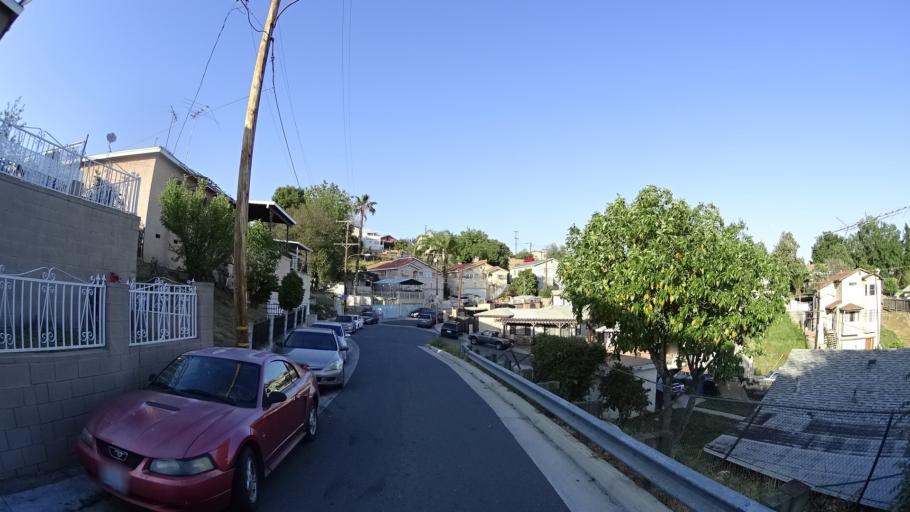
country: US
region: California
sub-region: Los Angeles County
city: Belvedere
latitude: 34.0504
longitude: -118.1839
